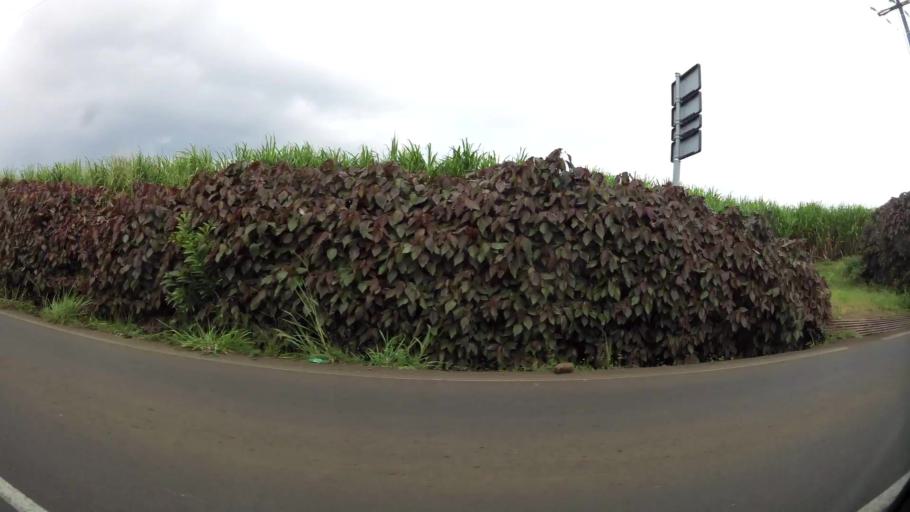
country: RE
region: Reunion
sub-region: Reunion
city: Sainte-Suzanne
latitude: -20.9075
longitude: 55.5987
